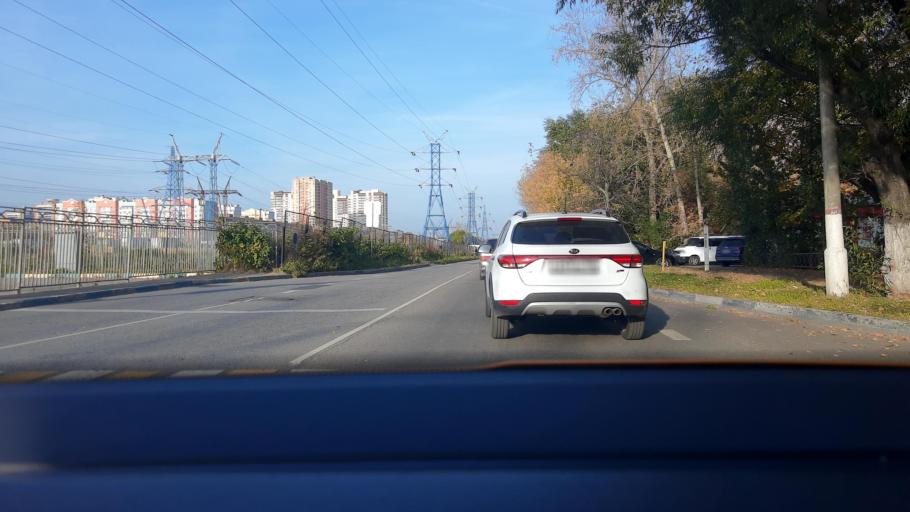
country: RU
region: Moskovskaya
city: Reutov
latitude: 55.7624
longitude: 37.8479
